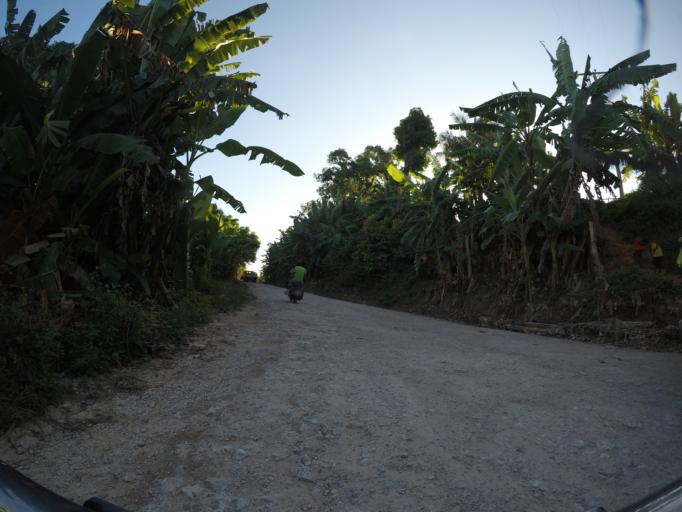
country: TZ
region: Pemba South
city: Uwelini
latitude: -5.3759
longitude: 39.6694
